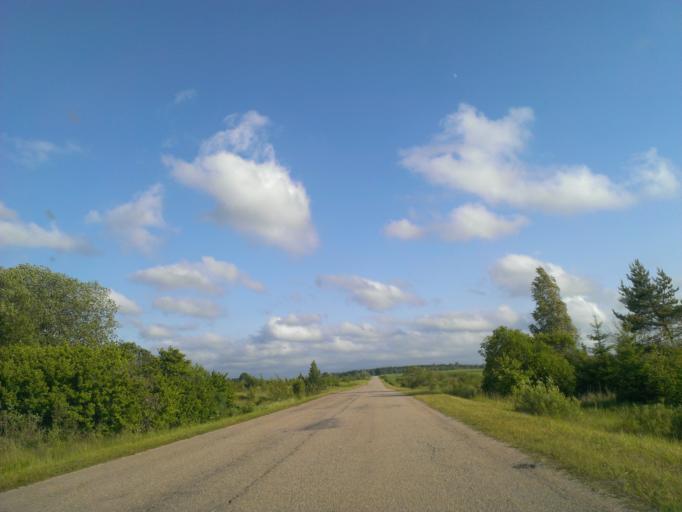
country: LV
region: Aizpute
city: Aizpute
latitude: 56.7866
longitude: 21.5145
